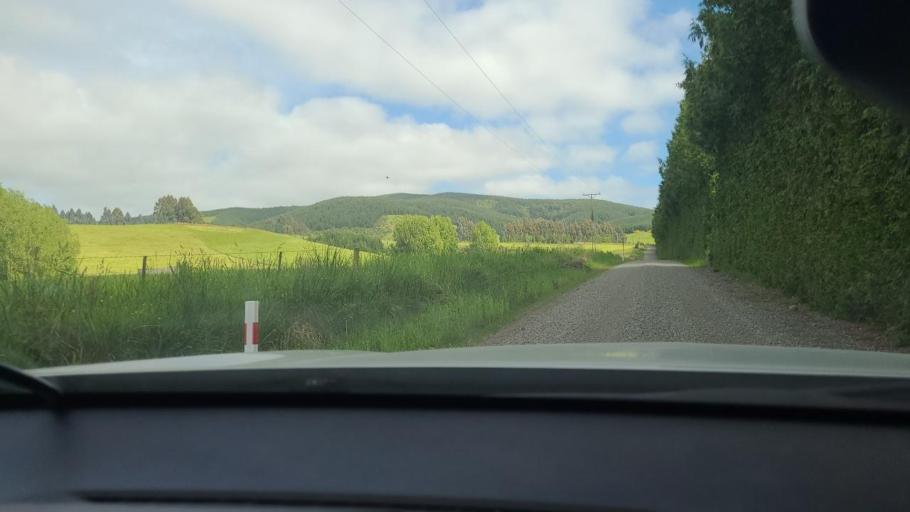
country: NZ
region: Southland
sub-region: Southland District
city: Winton
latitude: -45.9208
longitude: 168.0813
